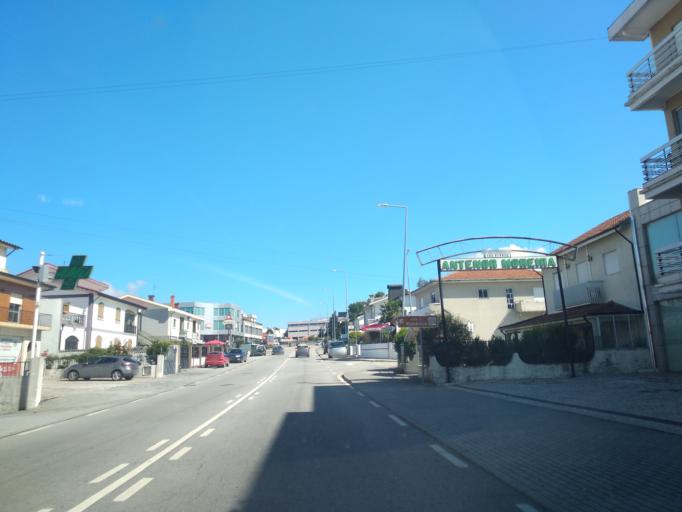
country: PT
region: Porto
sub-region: Pacos de Ferreira
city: Freamunde
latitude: 41.2813
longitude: -8.3332
